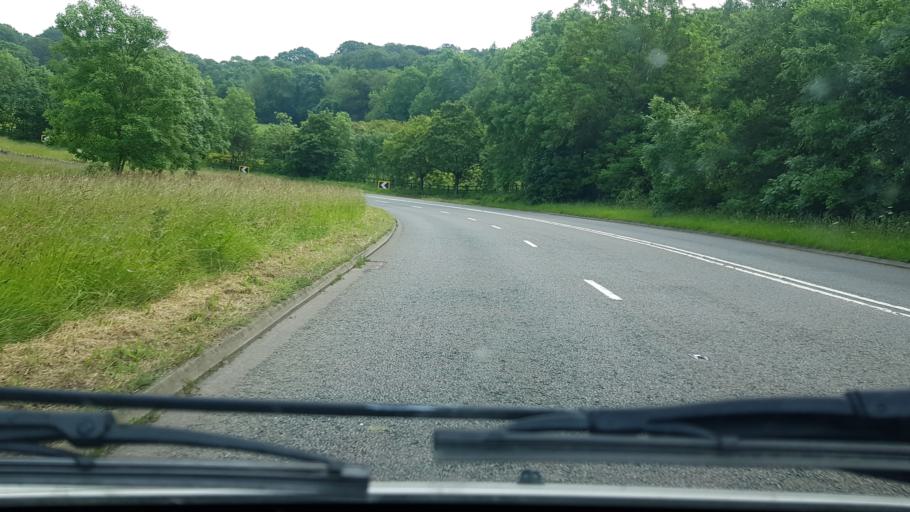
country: GB
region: England
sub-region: Worcestershire
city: Broadway
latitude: 52.0316
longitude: -1.8390
